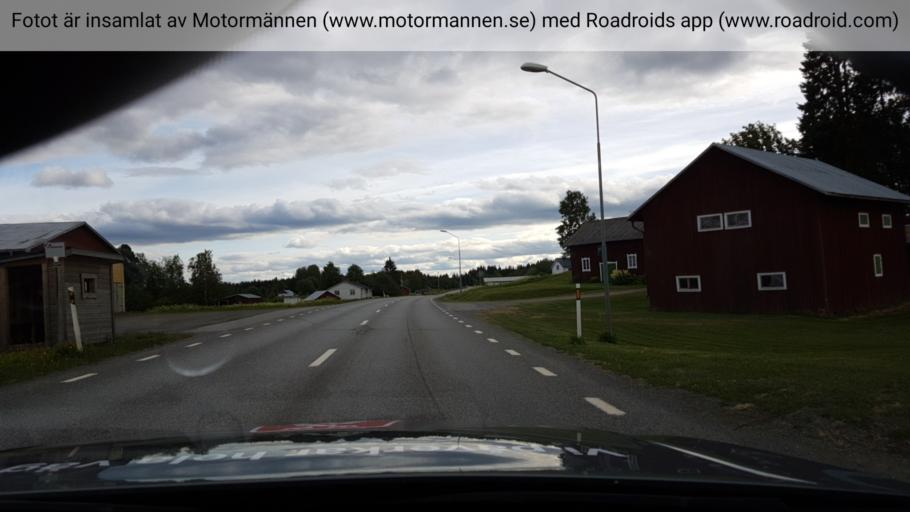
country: SE
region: Jaemtland
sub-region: Stroemsunds Kommun
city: Stroemsund
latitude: 63.4973
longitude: 15.2561
